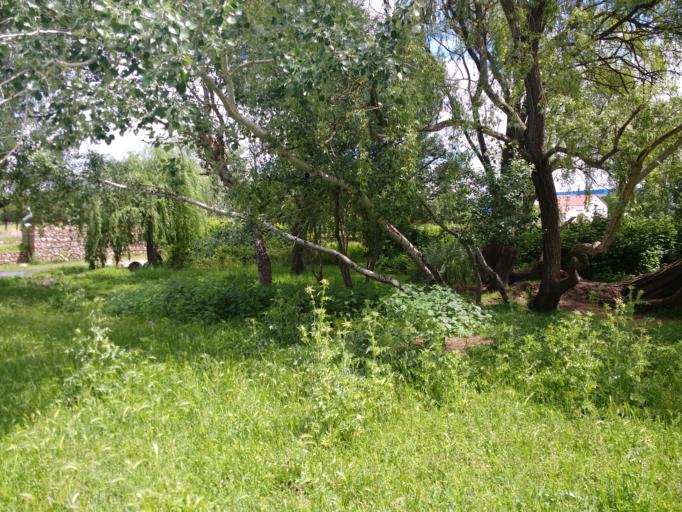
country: ES
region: Catalonia
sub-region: Provincia de Barcelona
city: Polinya
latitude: 41.5610
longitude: 2.1741
